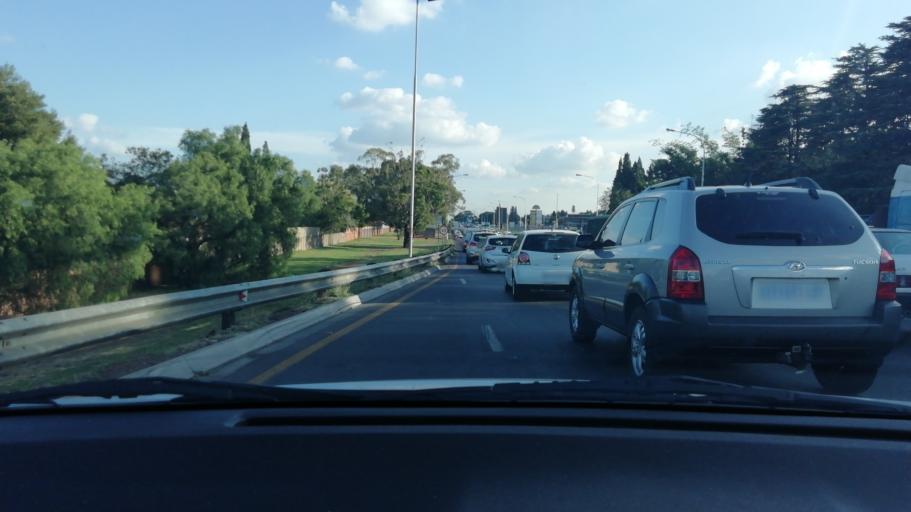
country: ZA
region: Gauteng
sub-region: Ekurhuleni Metropolitan Municipality
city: Boksburg
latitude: -26.1752
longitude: 28.2803
